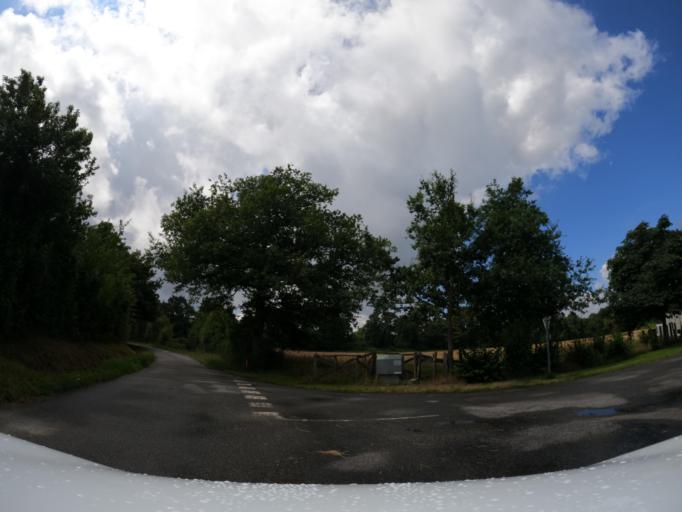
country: FR
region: Pays de la Loire
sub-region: Departement de la Loire-Atlantique
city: Saint-Mars-du-Desert
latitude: 47.3836
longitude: -1.4009
